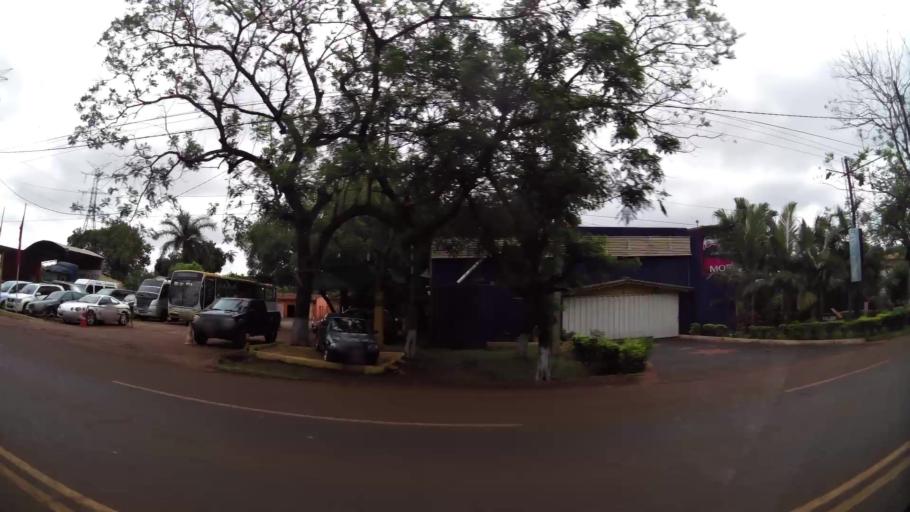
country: PY
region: Alto Parana
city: Ciudad del Este
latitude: -25.4255
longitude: -54.6378
